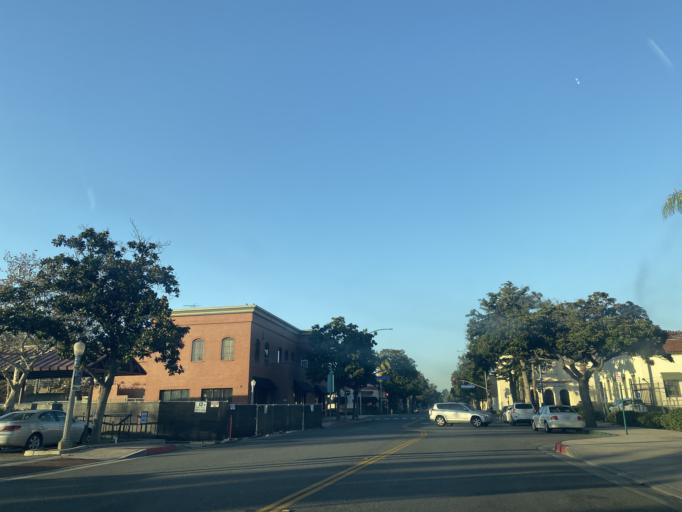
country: US
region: California
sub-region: Orange County
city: Fullerton
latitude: 33.8696
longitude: -117.9221
